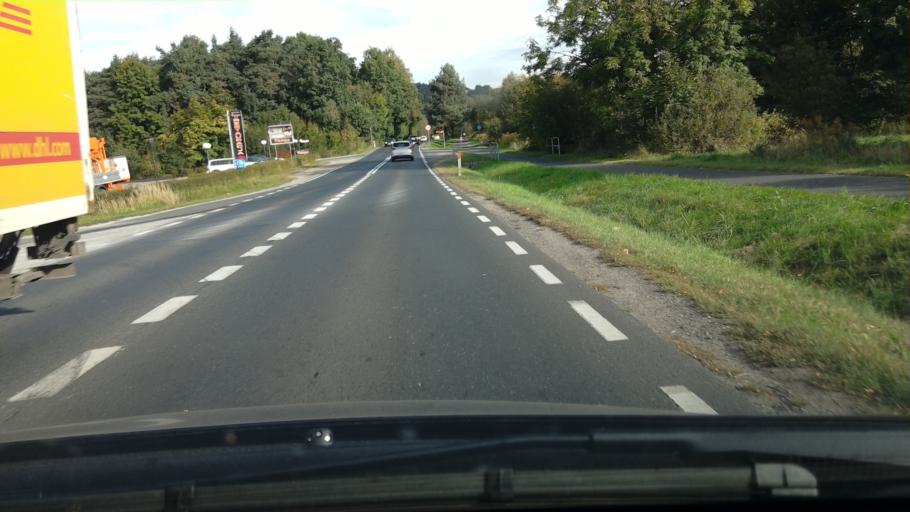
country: PL
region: Lower Silesian Voivodeship
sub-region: Jelenia Gora
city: Jelenia Gora
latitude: 50.8780
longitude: 15.7589
